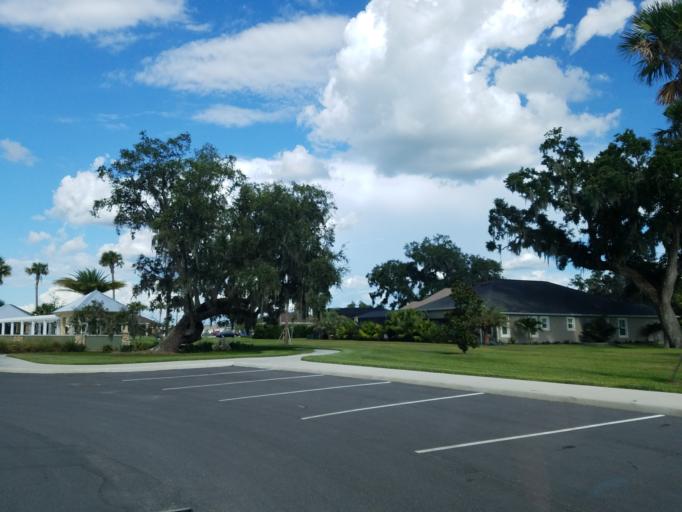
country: US
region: Florida
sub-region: Sumter County
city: Wildwood
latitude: 28.7985
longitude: -82.0376
